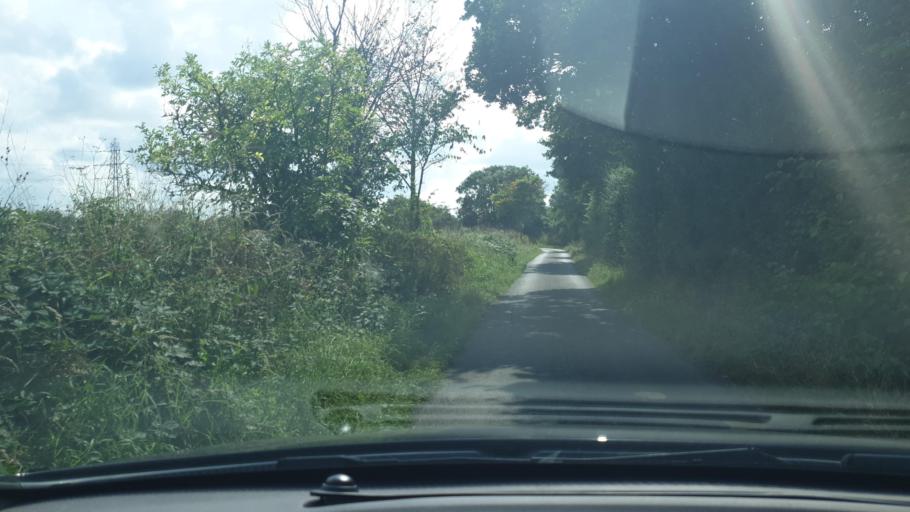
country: GB
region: England
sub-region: Essex
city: Manningtree
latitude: 51.9245
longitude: 1.0280
